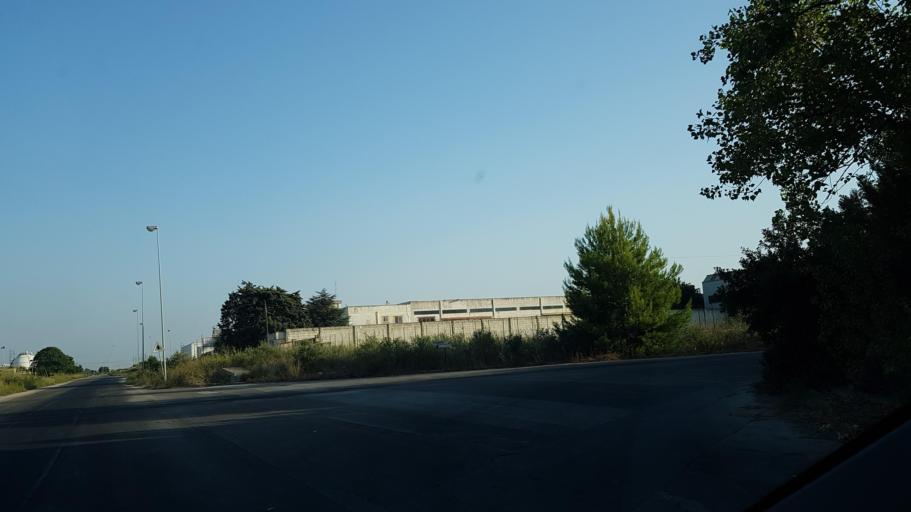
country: IT
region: Apulia
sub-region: Provincia di Brindisi
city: Materdomini
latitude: 40.6295
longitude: 17.9754
